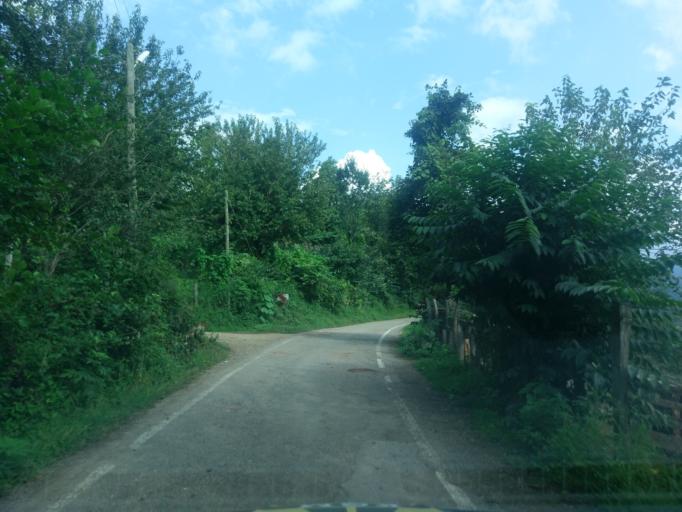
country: TR
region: Ordu
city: Camas
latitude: 40.9264
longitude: 37.6126
